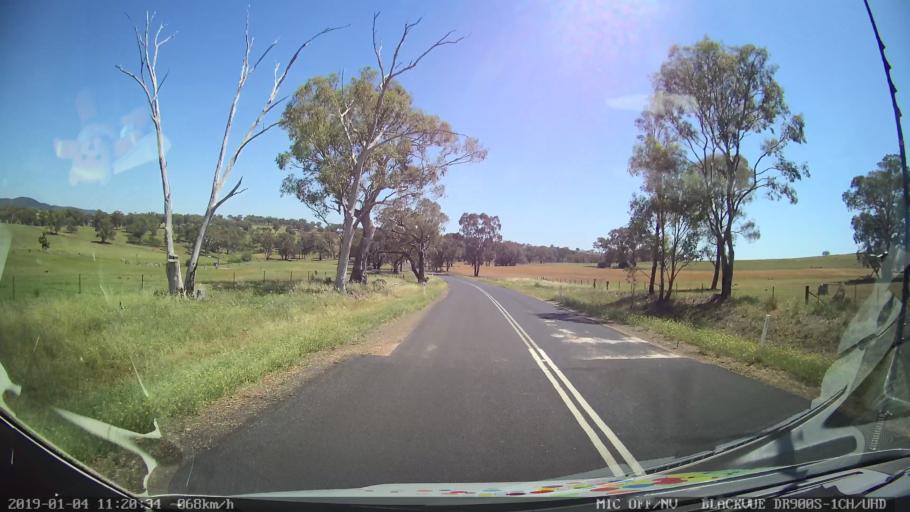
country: AU
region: New South Wales
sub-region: Cabonne
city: Molong
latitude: -33.1626
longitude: 148.7066
